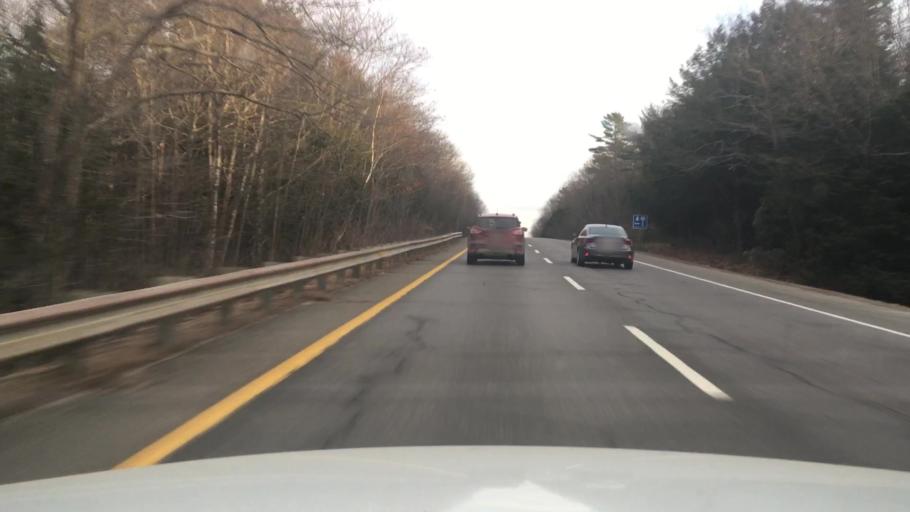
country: US
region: Maine
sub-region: Sagadahoc County
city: Bath
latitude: 43.9189
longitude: -69.8768
